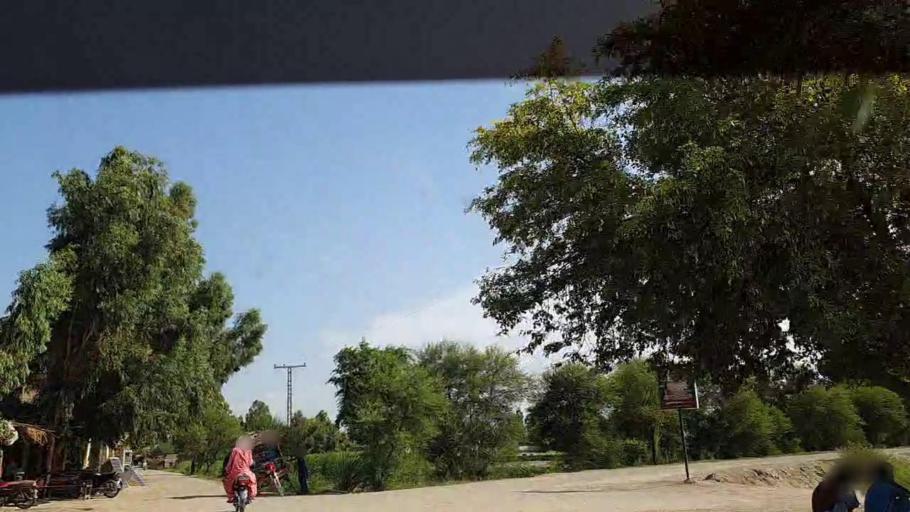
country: PK
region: Sindh
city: Adilpur
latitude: 27.9317
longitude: 69.2548
